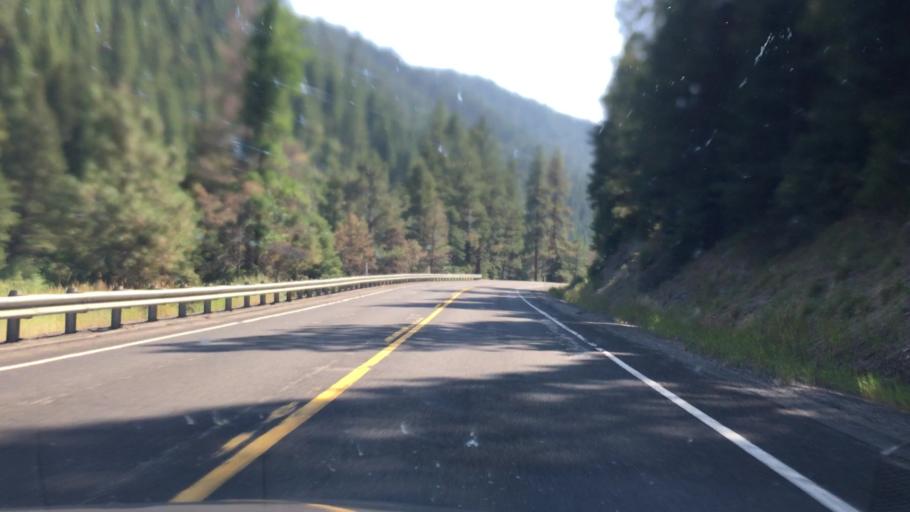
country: US
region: Idaho
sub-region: Valley County
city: Cascade
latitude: 44.2603
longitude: -116.0804
